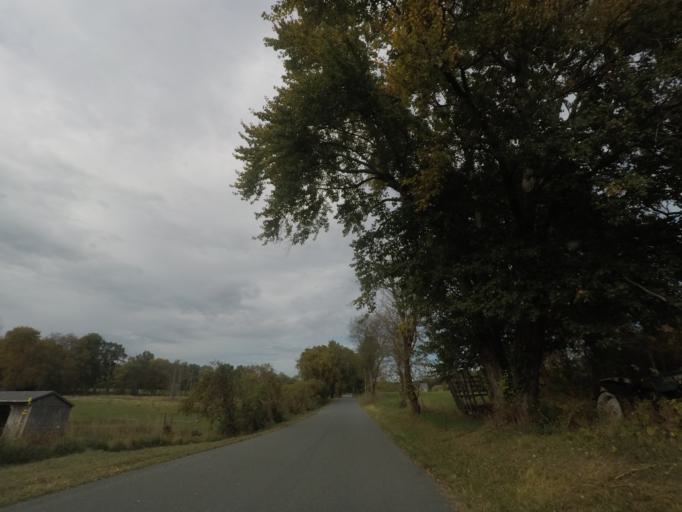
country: US
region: New York
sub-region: Rensselaer County
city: Nassau
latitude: 42.5444
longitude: -73.6250
